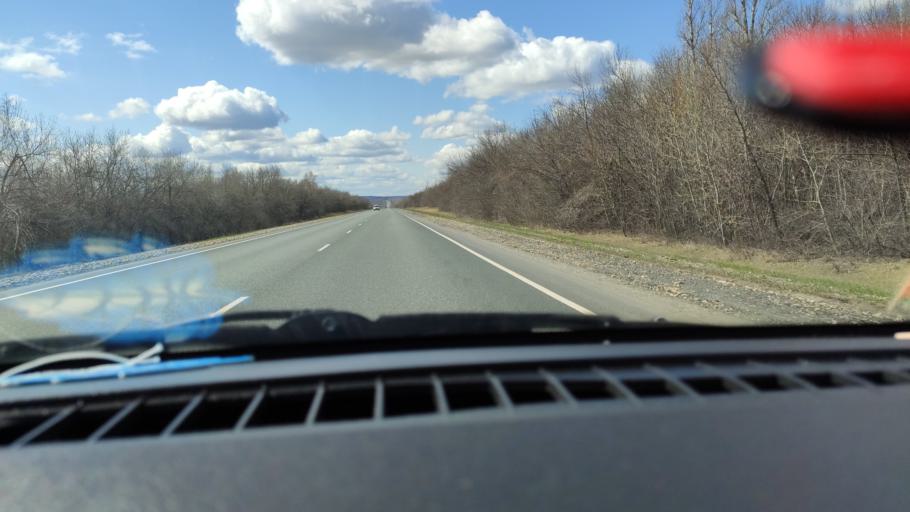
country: RU
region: Saratov
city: Khvalynsk
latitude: 52.5929
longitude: 48.1332
